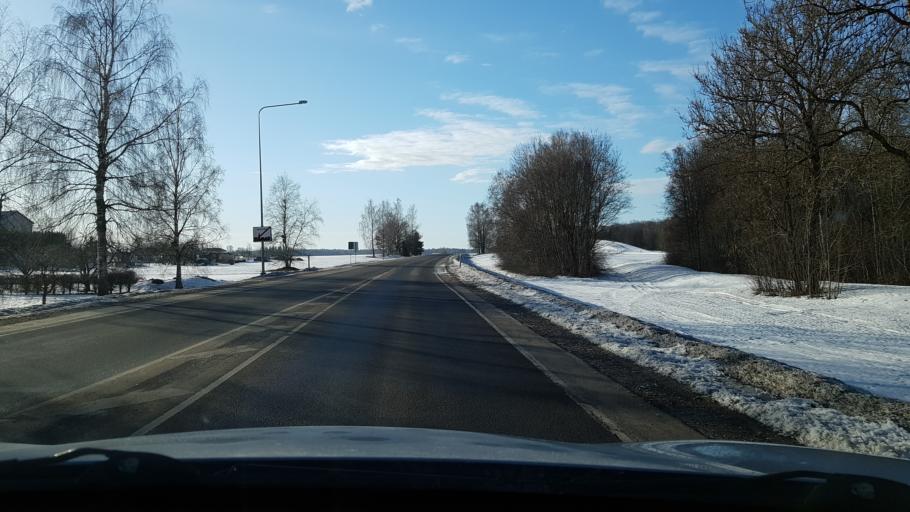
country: EE
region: Jogevamaa
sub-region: Poltsamaa linn
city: Poltsamaa
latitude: 58.7317
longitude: 25.7666
